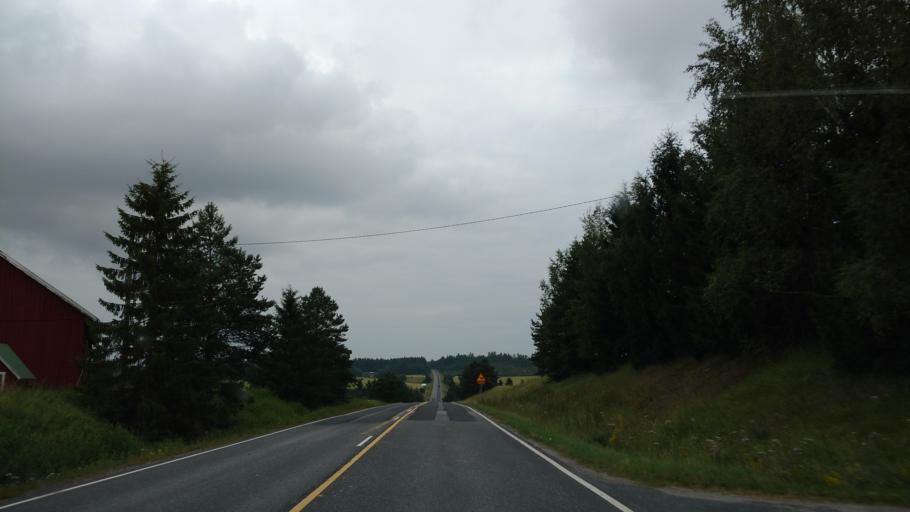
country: FI
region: Varsinais-Suomi
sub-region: Salo
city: Halikko
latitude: 60.4746
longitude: 23.0130
